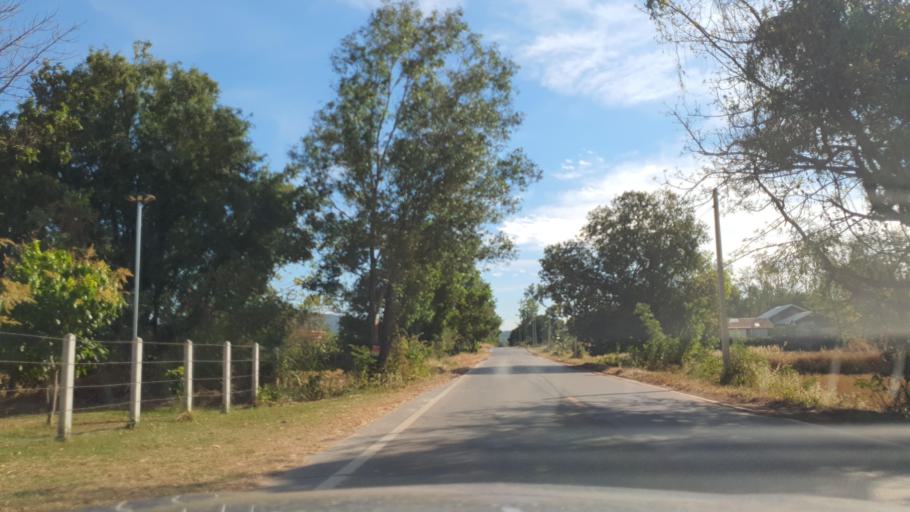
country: TH
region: Kalasin
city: Kuchinarai
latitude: 16.6009
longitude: 104.1351
